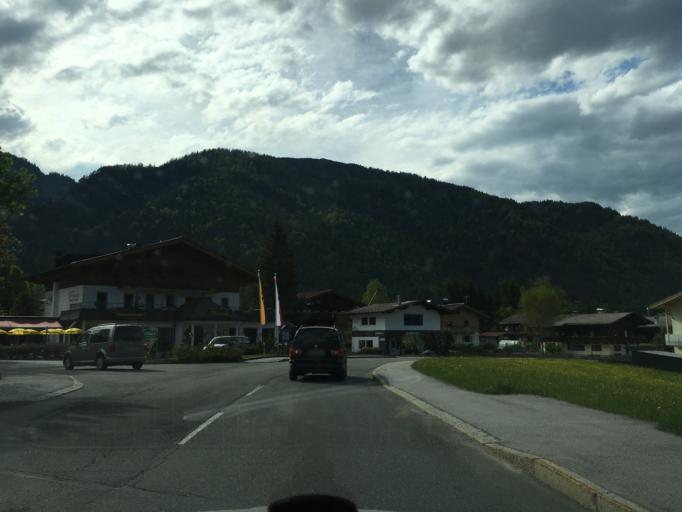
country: AT
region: Tyrol
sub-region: Politischer Bezirk Kitzbuhel
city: Fieberbrunn
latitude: 47.5258
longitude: 12.5741
